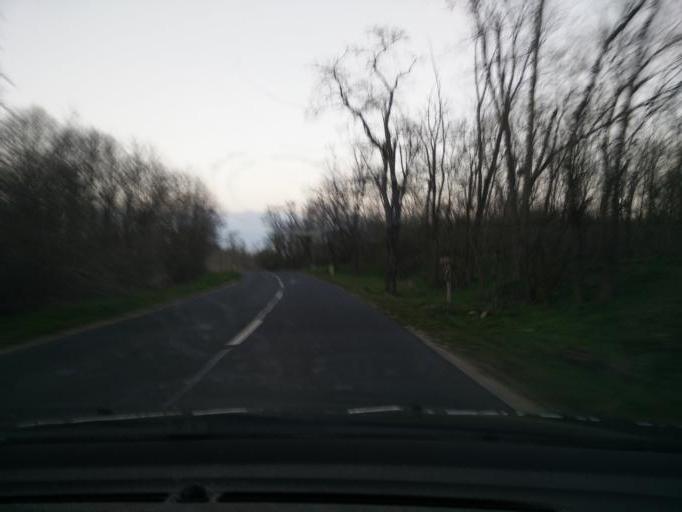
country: HU
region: Veszprem
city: Csabrendek
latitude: 47.0540
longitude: 17.3381
